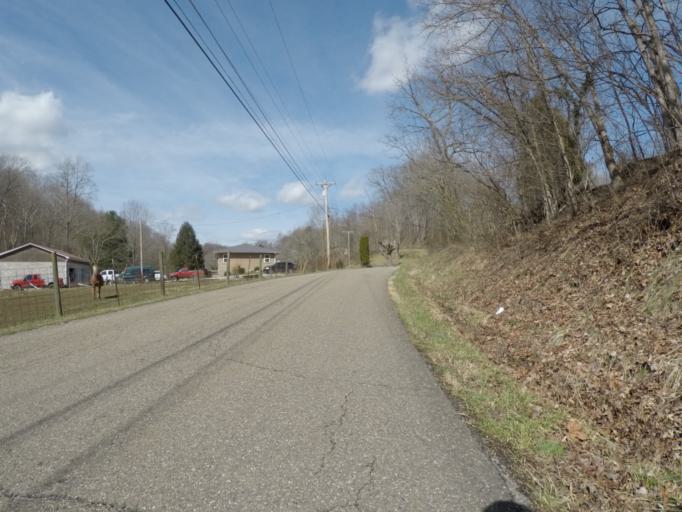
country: US
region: Ohio
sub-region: Lawrence County
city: Burlington
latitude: 38.4787
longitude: -82.5175
